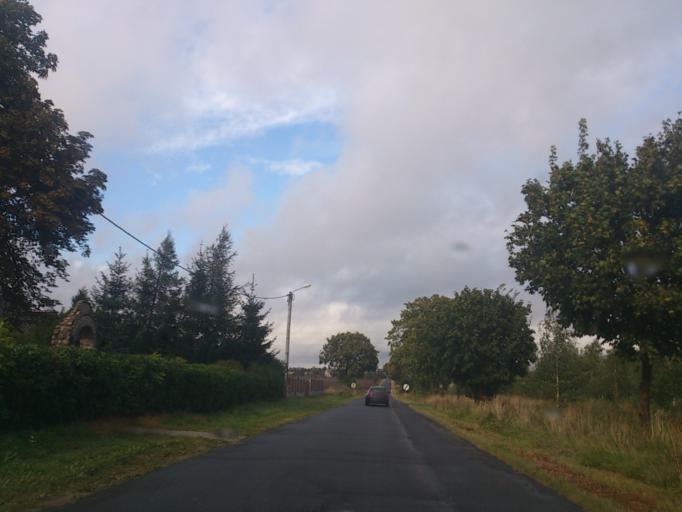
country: PL
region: Greater Poland Voivodeship
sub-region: Powiat poznanski
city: Pobiedziska
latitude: 52.4994
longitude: 17.3621
